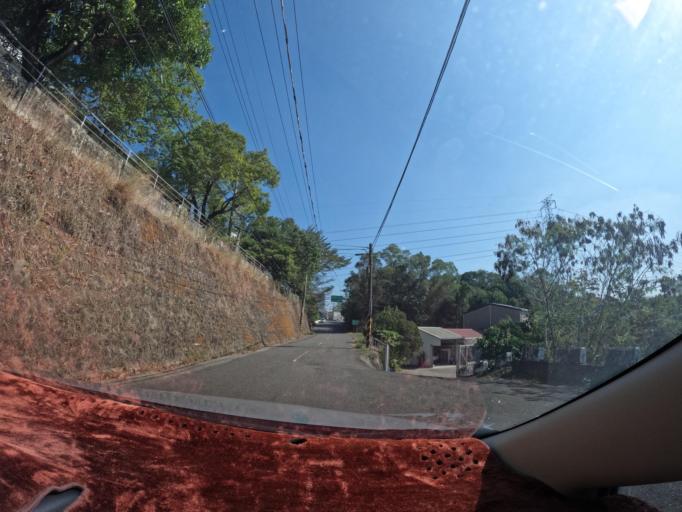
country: TW
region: Taiwan
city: Yujing
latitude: 23.0422
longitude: 120.3640
